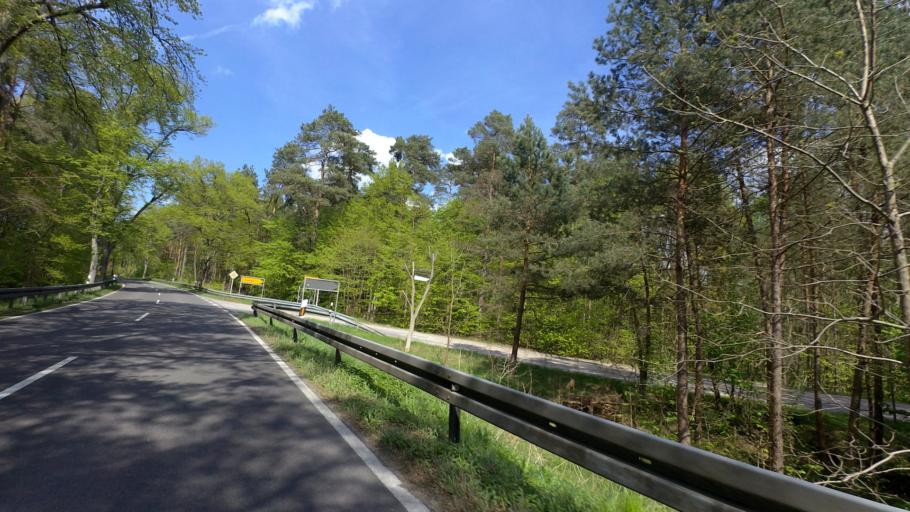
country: DE
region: Brandenburg
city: Milmersdorf
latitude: 53.0599
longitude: 13.6238
